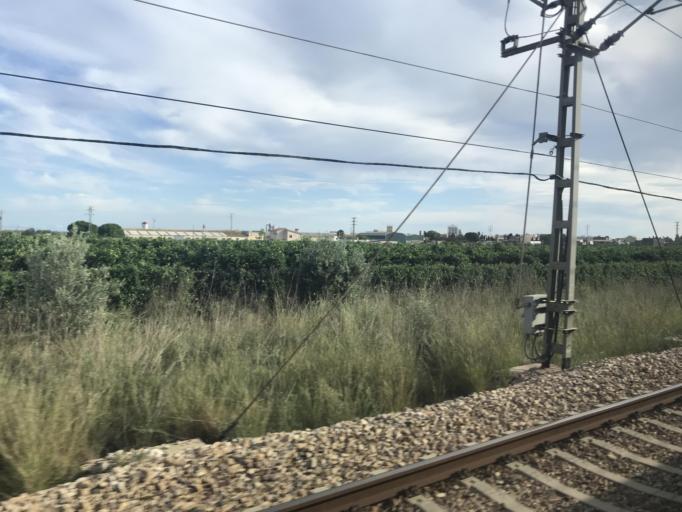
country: ES
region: Valencia
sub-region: Provincia de Castello
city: Benicarlo
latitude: 40.4345
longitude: 0.4212
